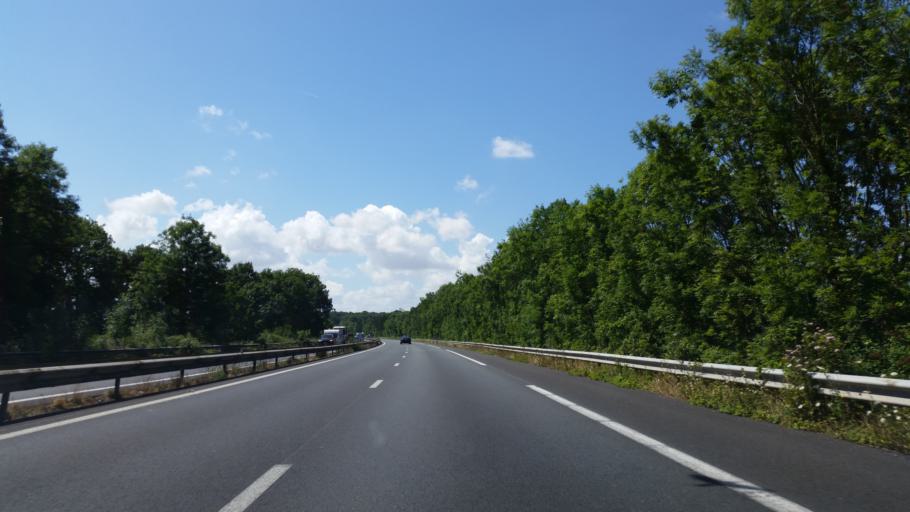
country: FR
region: Lower Normandy
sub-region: Departement du Calvados
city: Troarn
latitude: 49.2036
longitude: -0.1703
